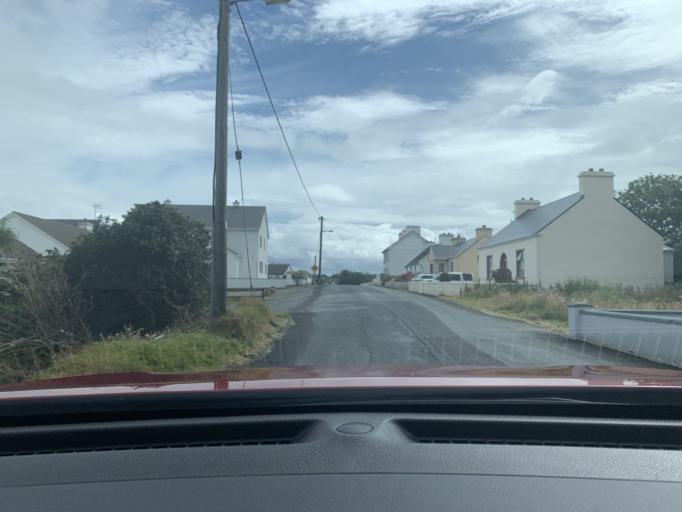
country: IE
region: Ulster
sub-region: County Donegal
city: Dungloe
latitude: 54.9535
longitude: -8.3633
